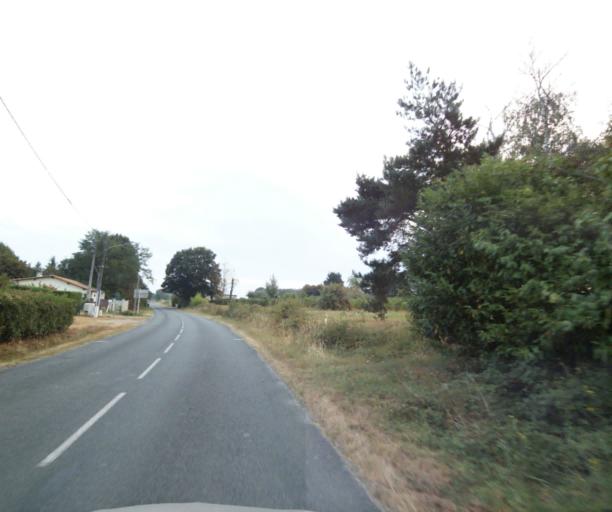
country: FR
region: Aquitaine
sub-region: Departement de la Gironde
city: La Sauve
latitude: 44.7513
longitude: -0.3324
